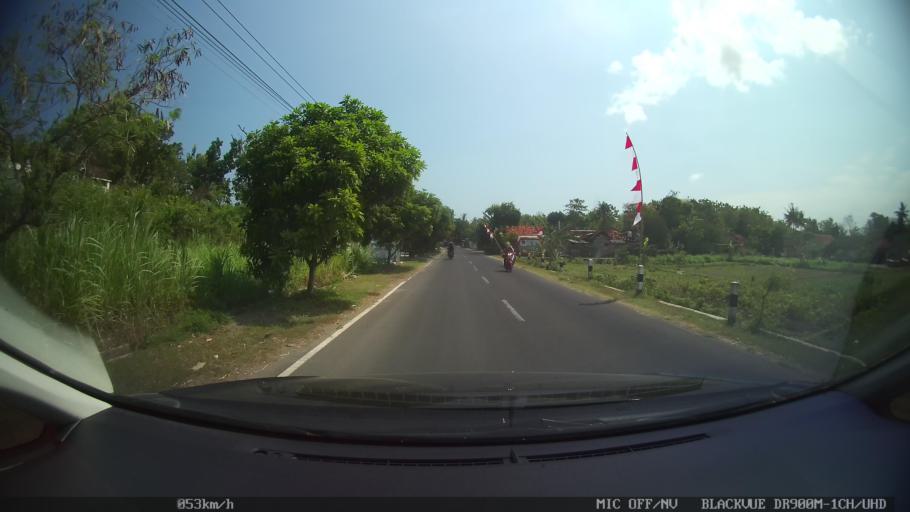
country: ID
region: Daerah Istimewa Yogyakarta
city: Pundong
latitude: -7.9877
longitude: 110.3223
